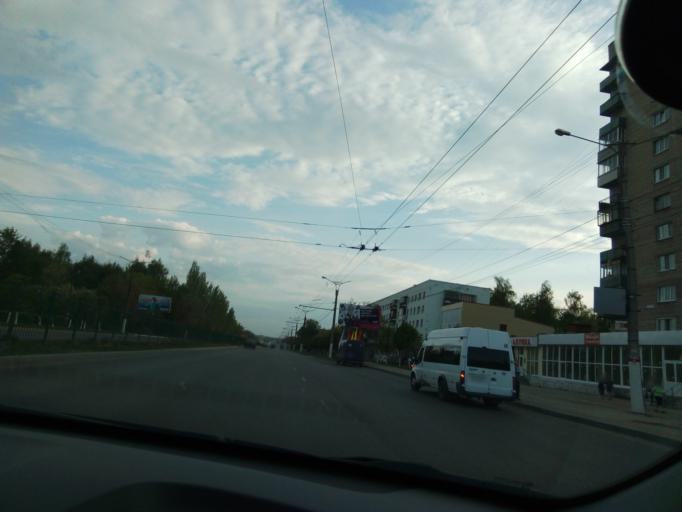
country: RU
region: Chuvashia
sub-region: Cheboksarskiy Rayon
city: Cheboksary
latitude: 56.1250
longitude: 47.2829
